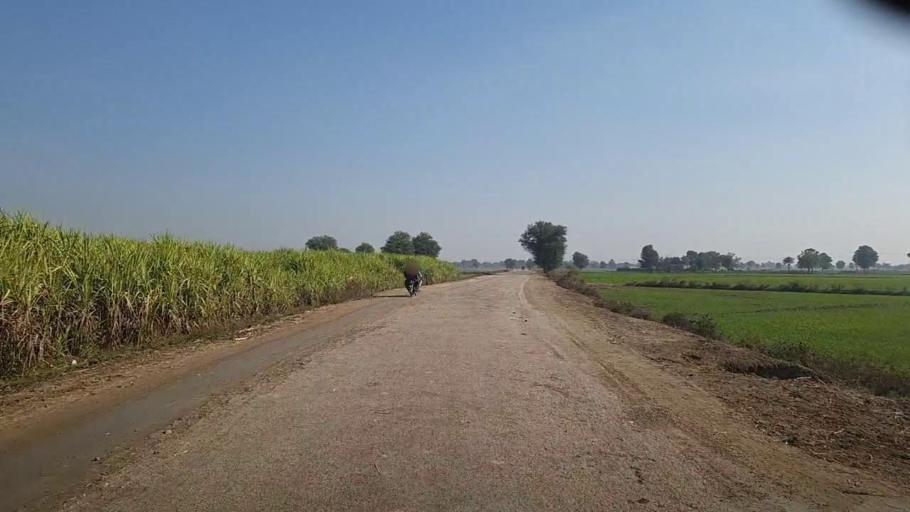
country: PK
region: Sindh
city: Darya Khan Marri
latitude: 26.6694
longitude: 68.3316
